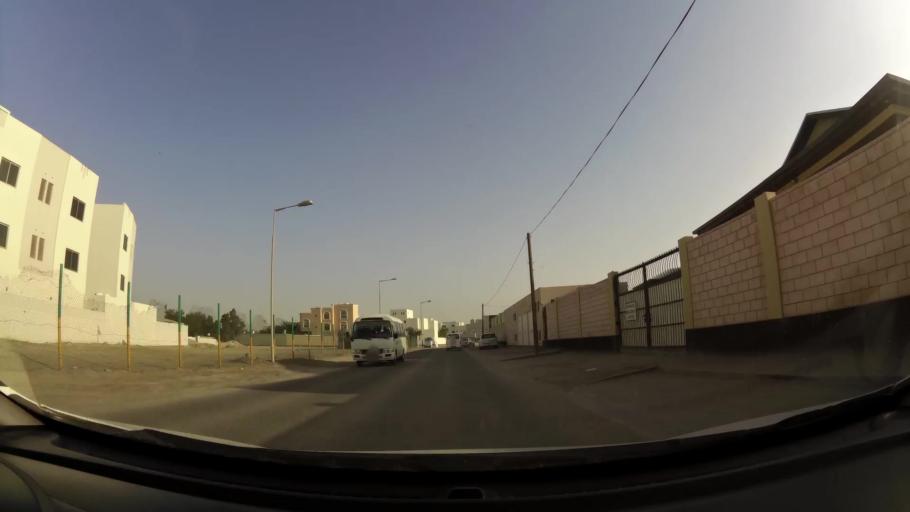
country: BH
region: Manama
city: Jidd Hafs
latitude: 26.2055
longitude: 50.5002
